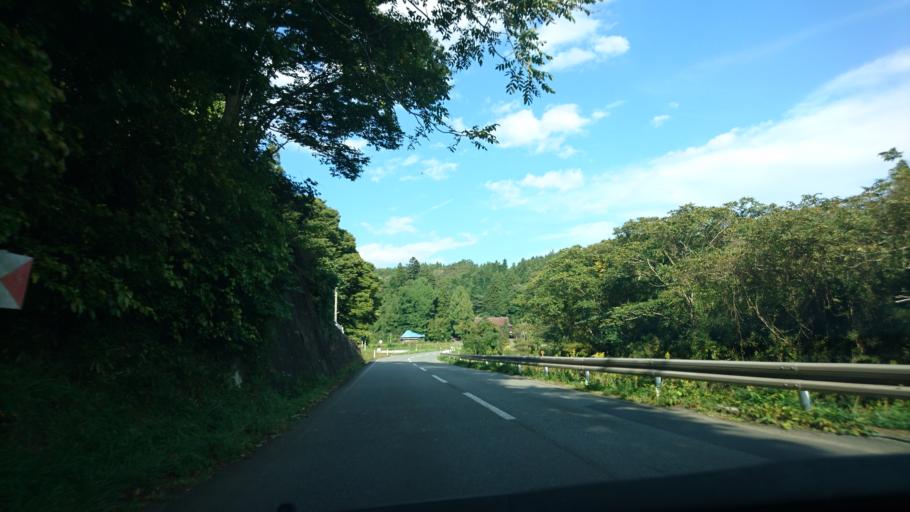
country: JP
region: Iwate
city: Ichinoseki
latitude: 38.8611
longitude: 141.3198
